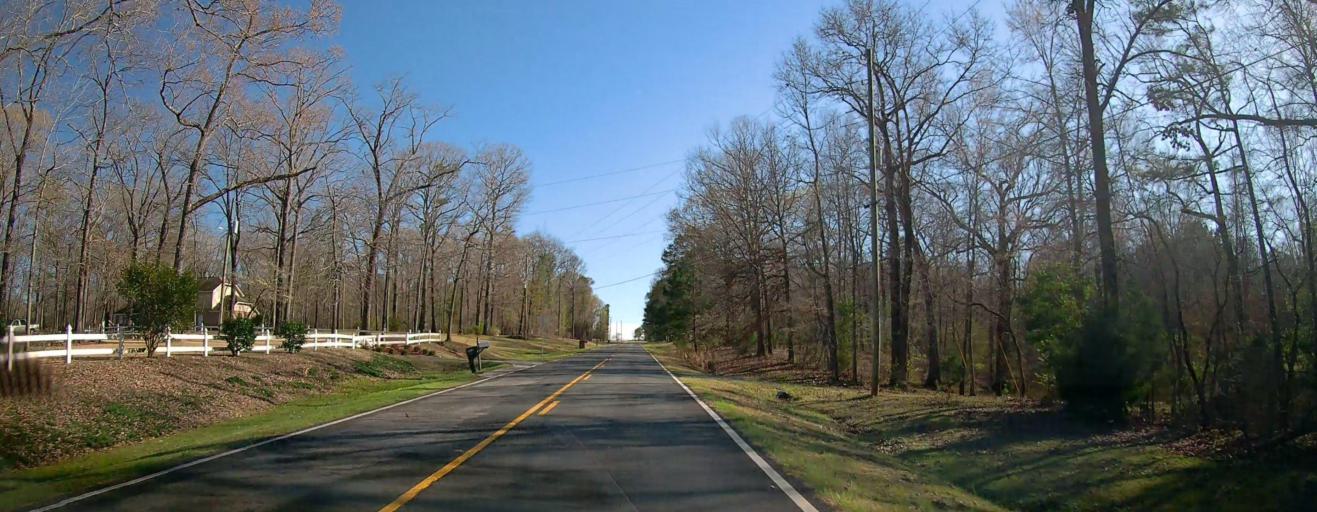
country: US
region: Georgia
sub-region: Peach County
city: Fort Valley
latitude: 32.5173
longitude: -83.9197
